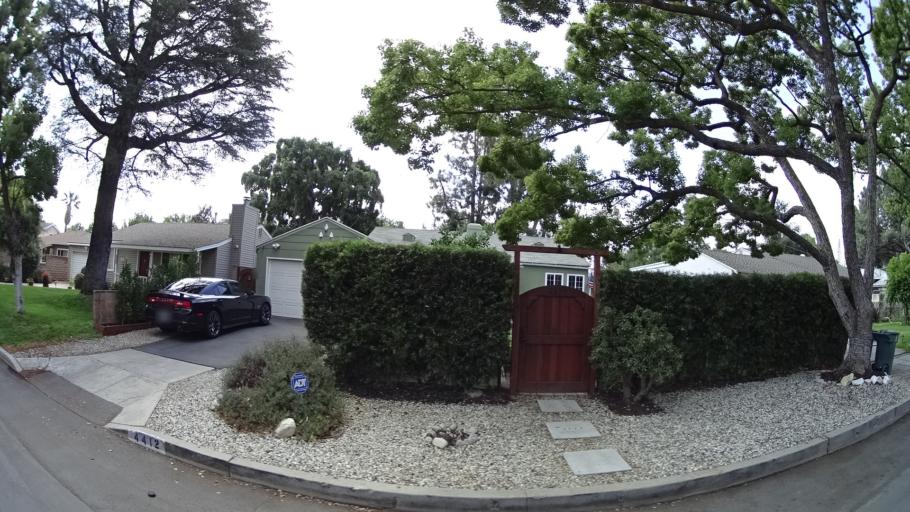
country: US
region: California
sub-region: Los Angeles County
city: Universal City
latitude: 34.1577
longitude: -118.3510
